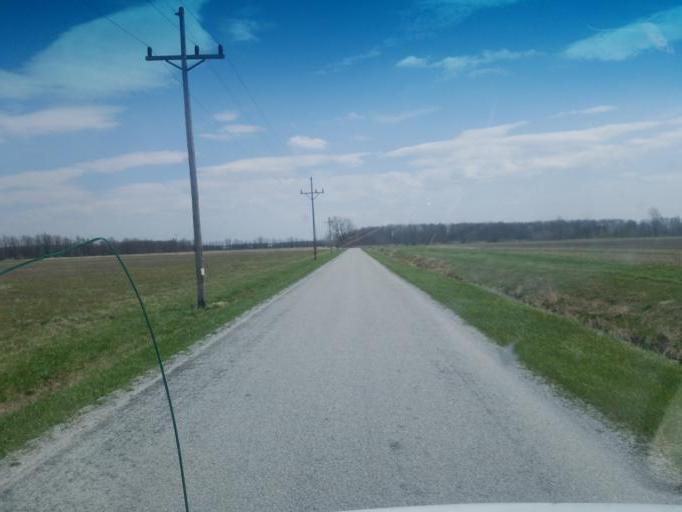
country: US
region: Ohio
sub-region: Hardin County
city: Forest
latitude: 40.7596
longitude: -83.5001
